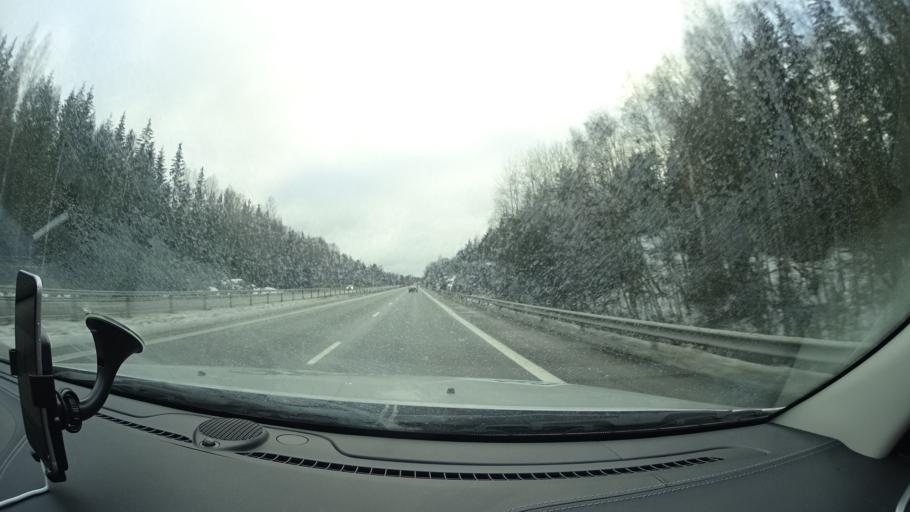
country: SE
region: OEstergoetland
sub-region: Odeshogs Kommun
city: OEdeshoeg
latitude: 58.1633
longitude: 14.5821
